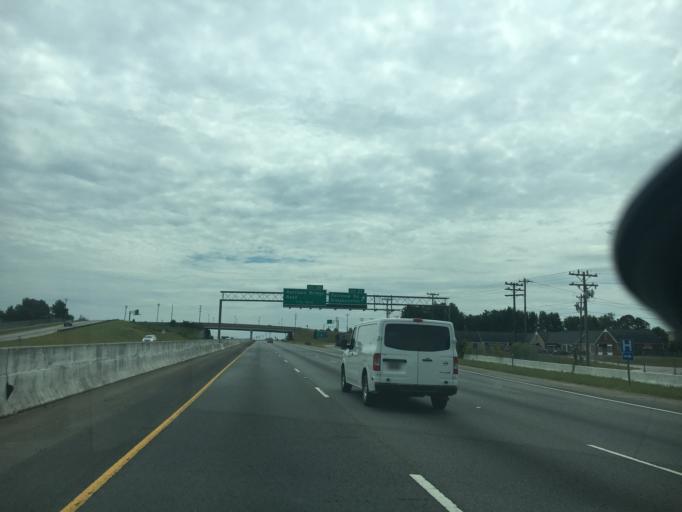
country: US
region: South Carolina
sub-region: Greenville County
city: Simpsonville
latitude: 34.7220
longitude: -82.2579
